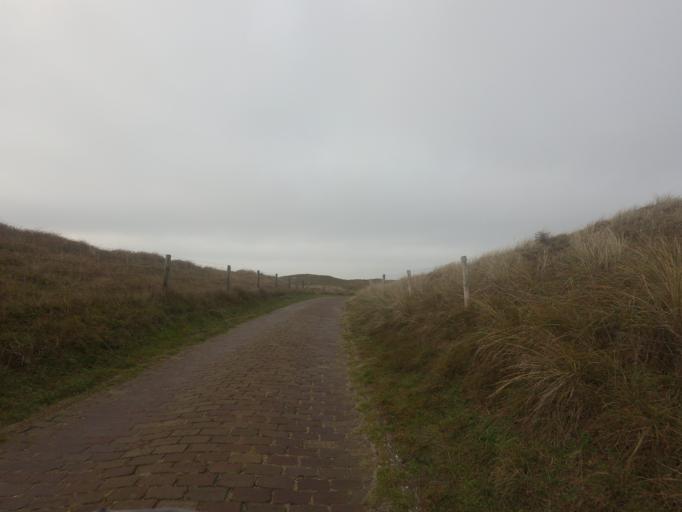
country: NL
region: North Holland
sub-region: Gemeente Texel
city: Den Burg
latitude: 53.1195
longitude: 4.8022
